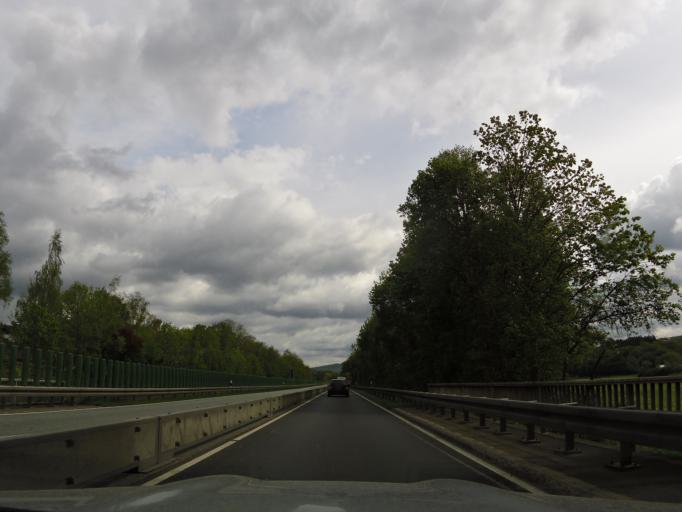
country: DE
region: Hesse
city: Selters
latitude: 50.5312
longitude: 8.3158
